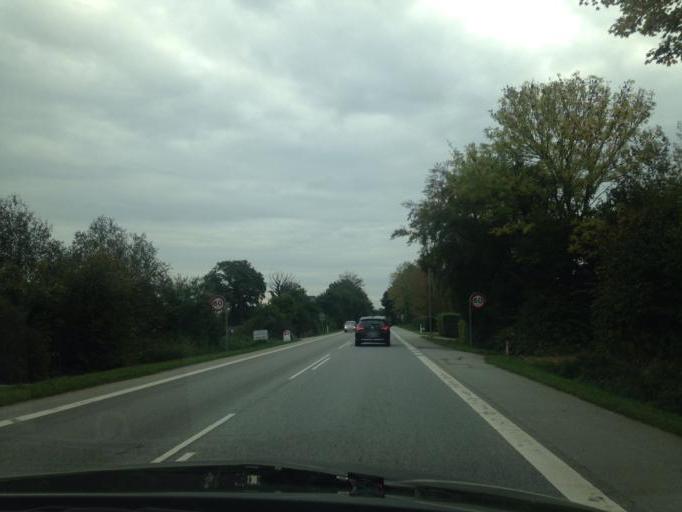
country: DK
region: South Denmark
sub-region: Haderslev Kommune
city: Haderslev
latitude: 55.2454
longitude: 9.4384
